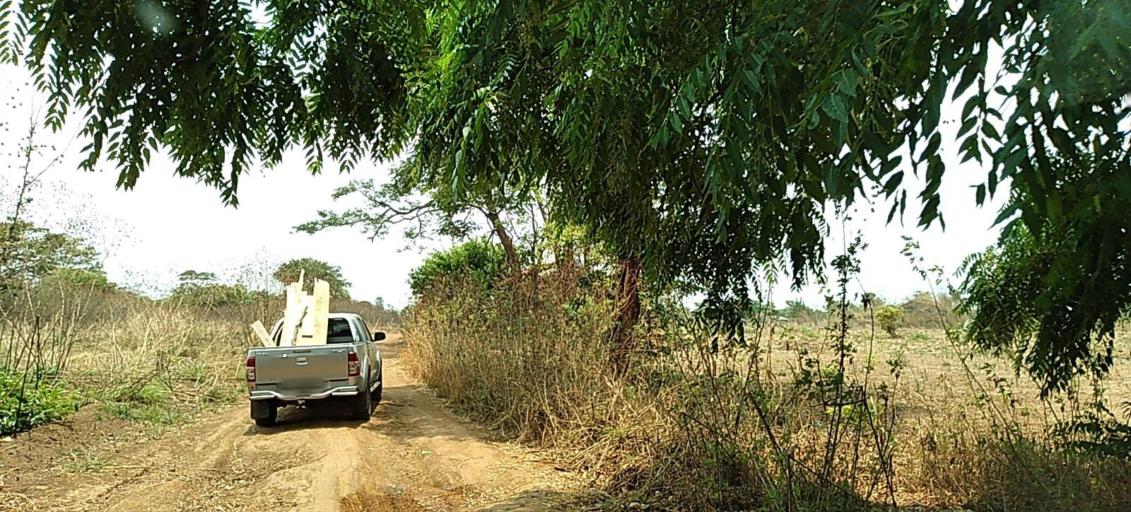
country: ZM
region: Copperbelt
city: Kalulushi
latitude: -12.7996
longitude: 28.0072
